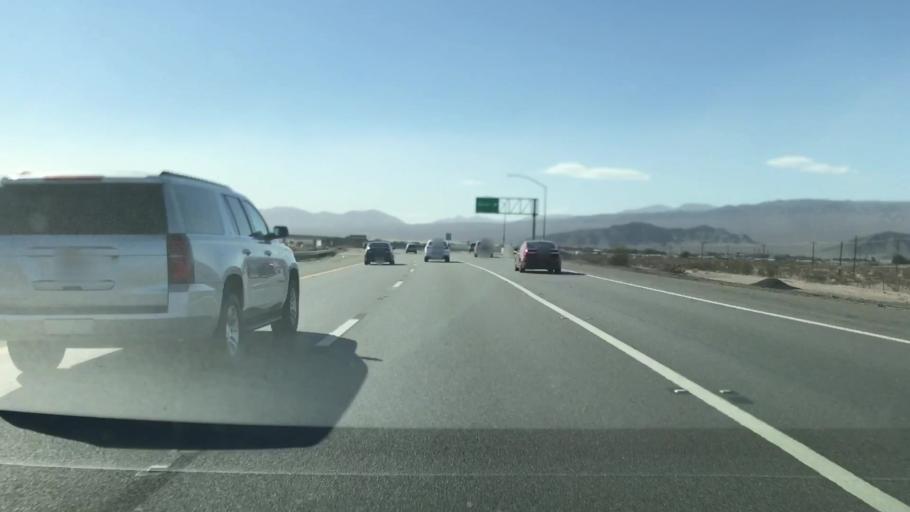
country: US
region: California
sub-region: San Bernardino County
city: Fort Irwin
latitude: 35.2860
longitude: -116.0438
